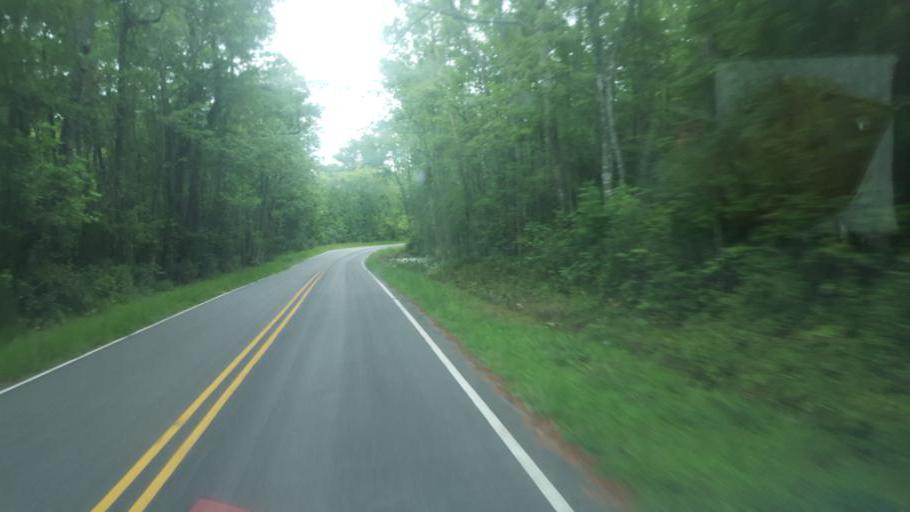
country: US
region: North Carolina
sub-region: Tyrrell County
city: Columbia
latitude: 35.9461
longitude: -76.3028
